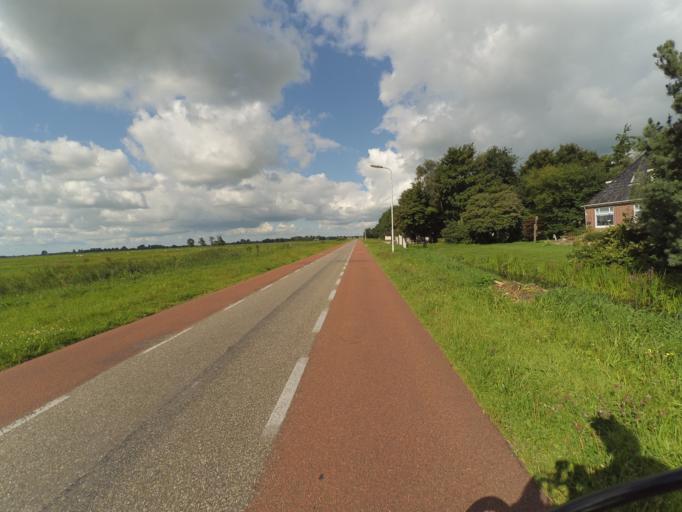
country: NL
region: Friesland
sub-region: Gemeente Dantumadiel
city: Rinsumageast
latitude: 53.2605
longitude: 5.9501
